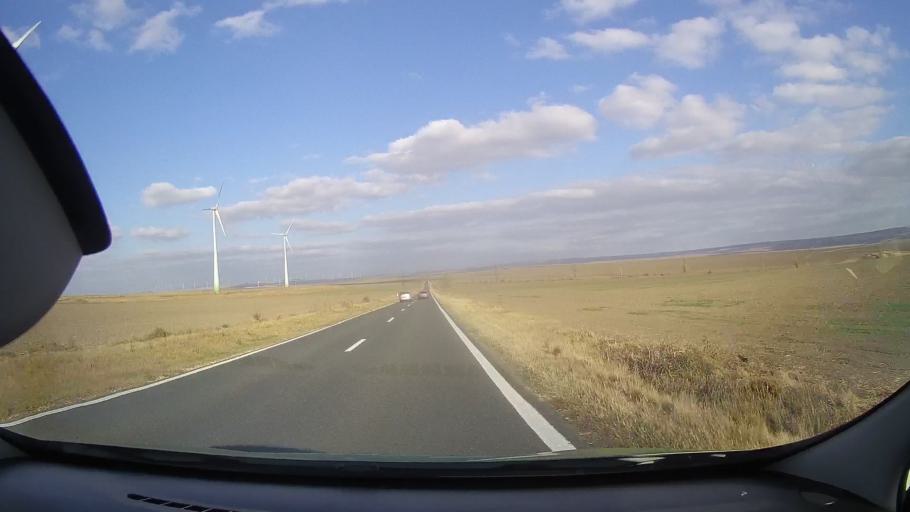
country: RO
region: Tulcea
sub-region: Comuna Topolog
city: Topolog
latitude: 44.8216
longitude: 28.2658
